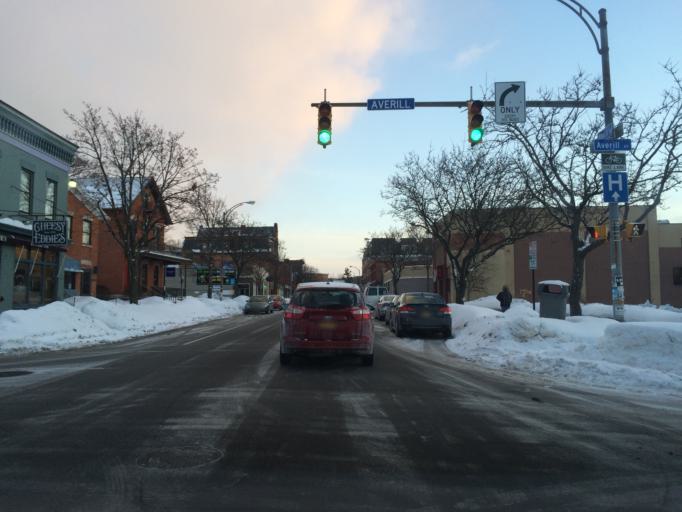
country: US
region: New York
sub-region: Monroe County
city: Rochester
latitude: 43.1440
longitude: -77.6049
